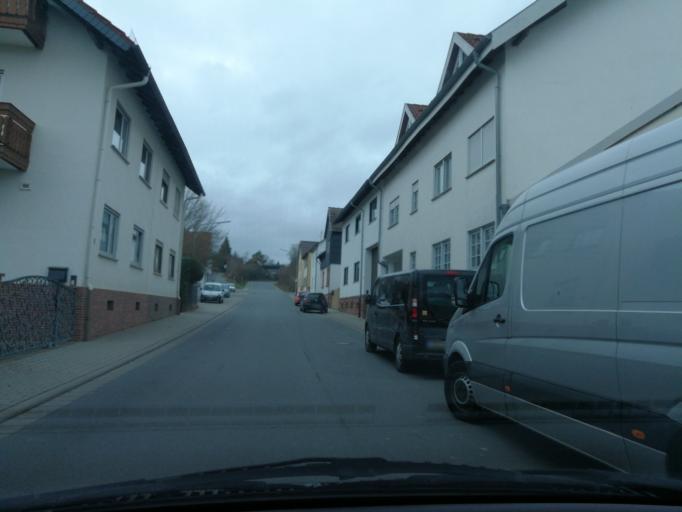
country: DE
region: Hesse
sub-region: Regierungsbezirk Darmstadt
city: Rossdorf
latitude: 49.8447
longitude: 8.7918
